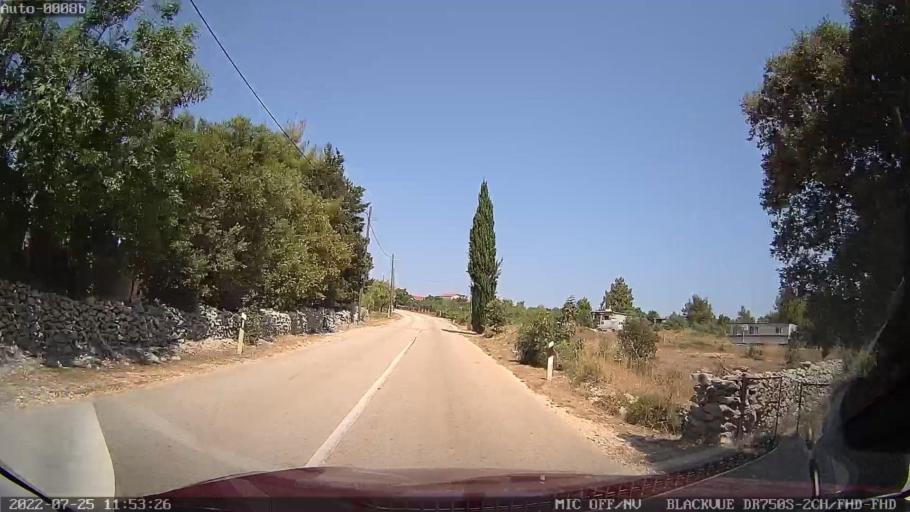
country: HR
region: Zadarska
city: Vrsi
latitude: 44.2559
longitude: 15.2349
